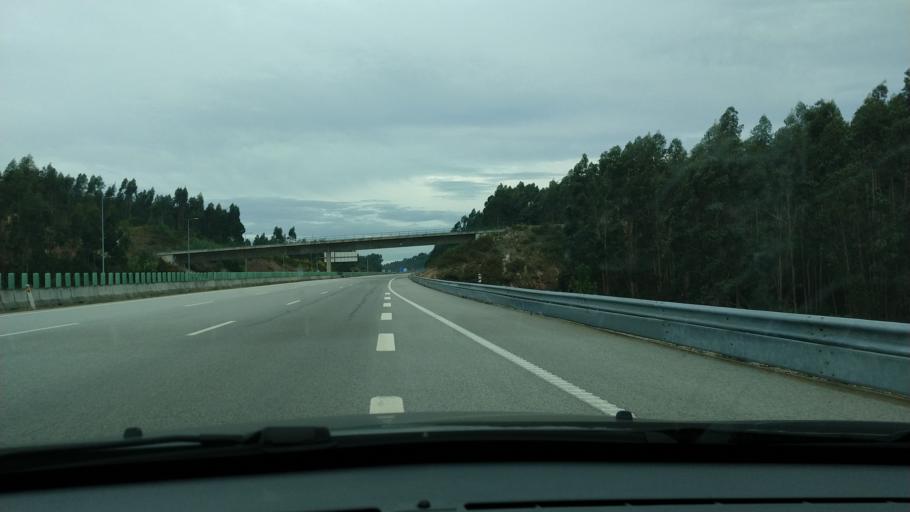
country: PT
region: Coimbra
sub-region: Figueira da Foz
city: Alhadas
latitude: 40.1601
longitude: -8.7774
